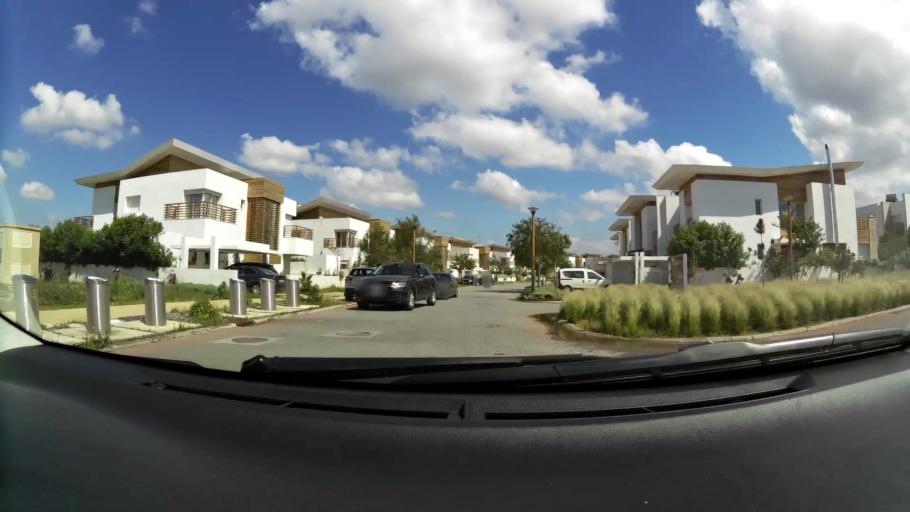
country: MA
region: Grand Casablanca
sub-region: Nouaceur
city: Bouskoura
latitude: 33.4872
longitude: -7.5969
